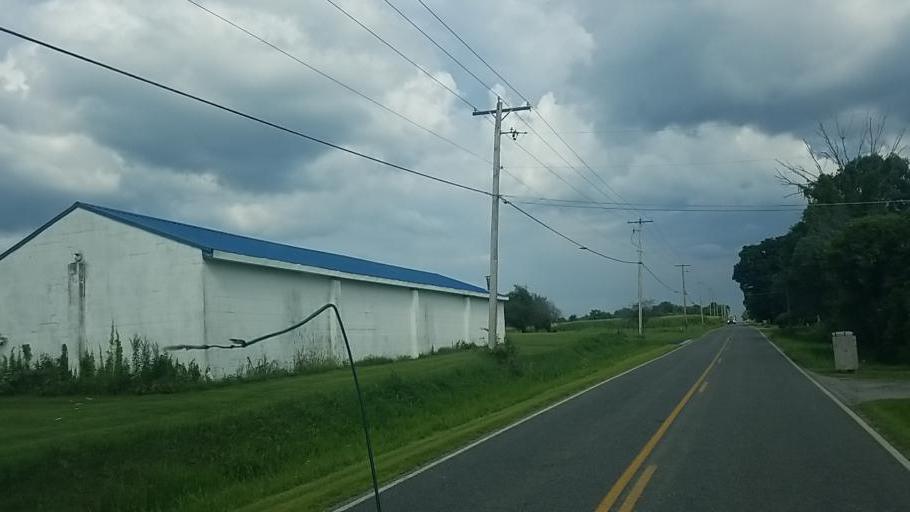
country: US
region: Ohio
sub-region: Medina County
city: Westfield Center
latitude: 41.0121
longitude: -81.9235
